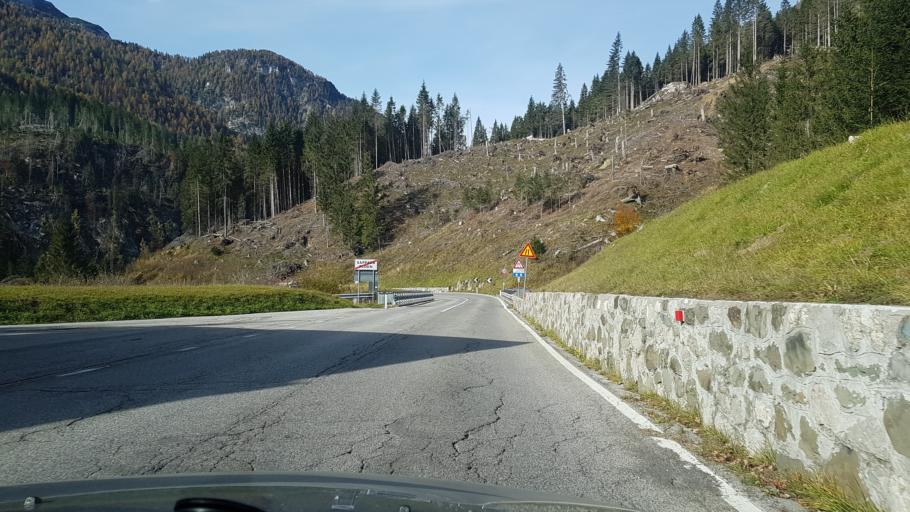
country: IT
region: Veneto
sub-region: Provincia di Belluno
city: Sappada
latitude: 46.5665
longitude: 12.6648
